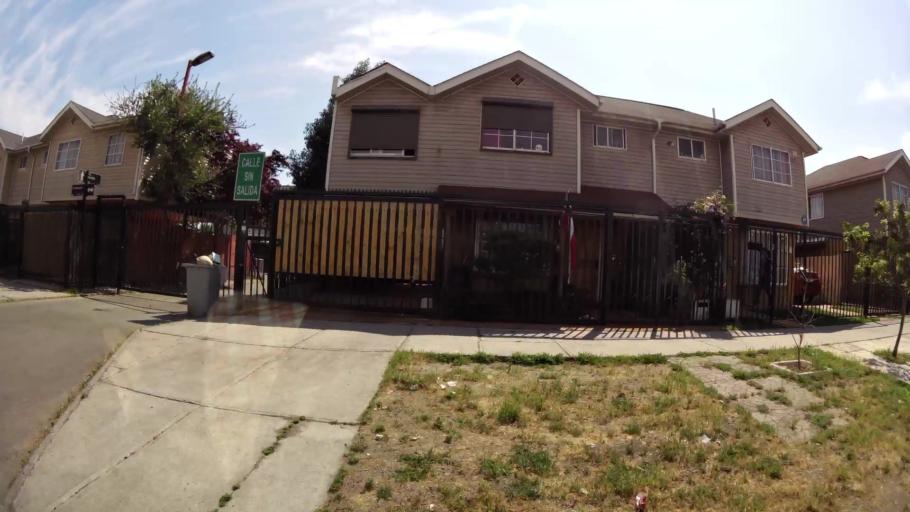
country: CL
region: Santiago Metropolitan
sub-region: Provincia de Cordillera
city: Puente Alto
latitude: -33.5926
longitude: -70.5902
